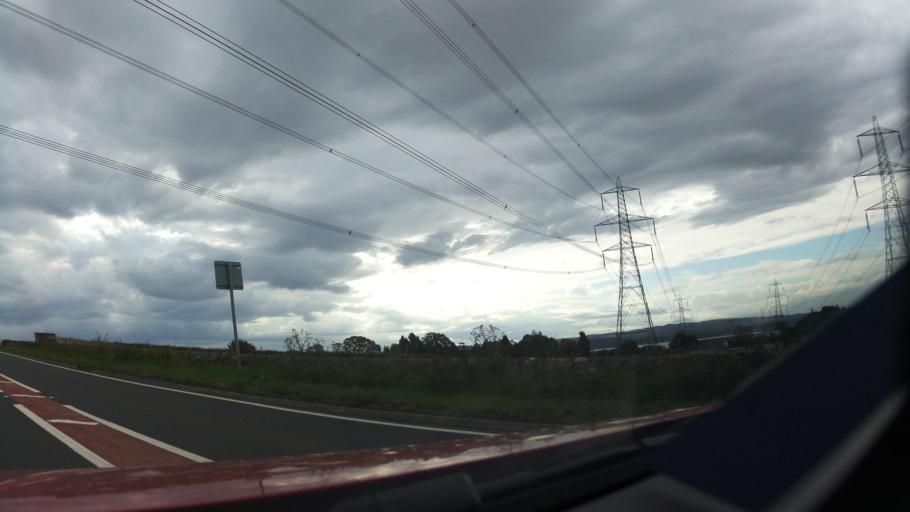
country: GB
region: Scotland
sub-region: Fife
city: Kincardine
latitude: 56.0646
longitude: -3.6892
